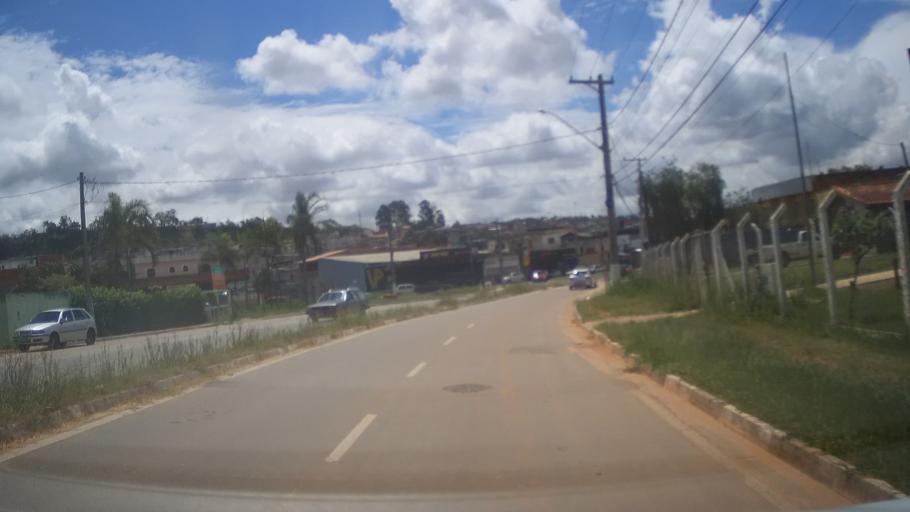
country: BR
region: Sao Paulo
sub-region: Campo Limpo Paulista
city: Campo Limpo Paulista
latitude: -23.2129
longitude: -46.7581
